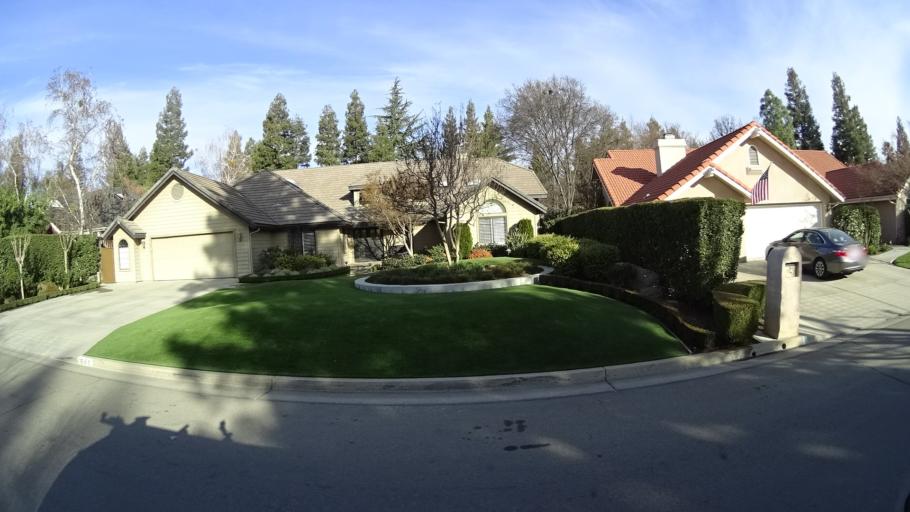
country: US
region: California
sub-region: Fresno County
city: Clovis
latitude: 36.8691
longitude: -119.7729
